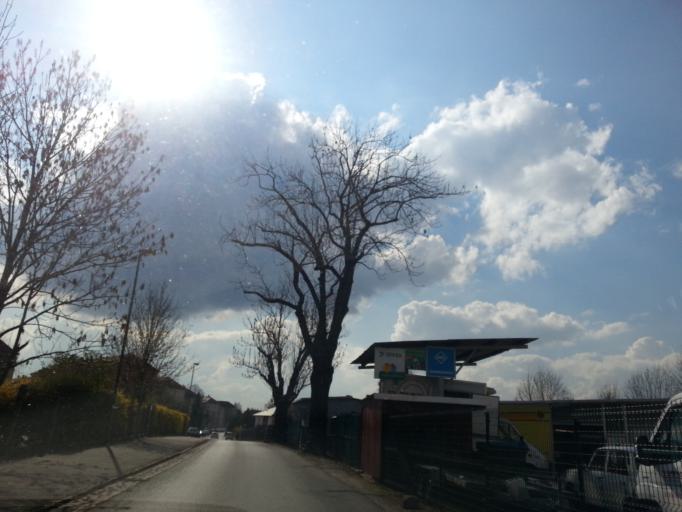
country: DE
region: Saxony
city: Dresden
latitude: 51.0897
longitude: 13.7228
